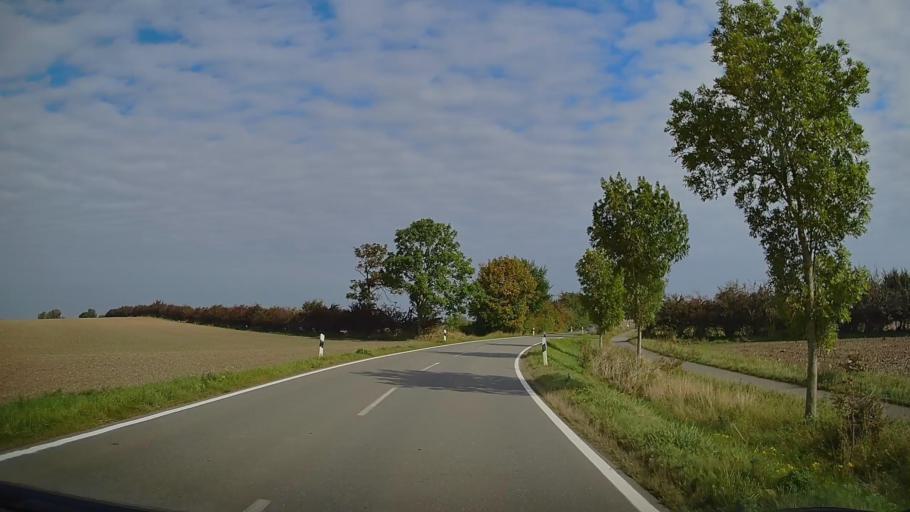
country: DE
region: Schleswig-Holstein
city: Gremersdorf
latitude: 54.3513
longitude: 10.9173
